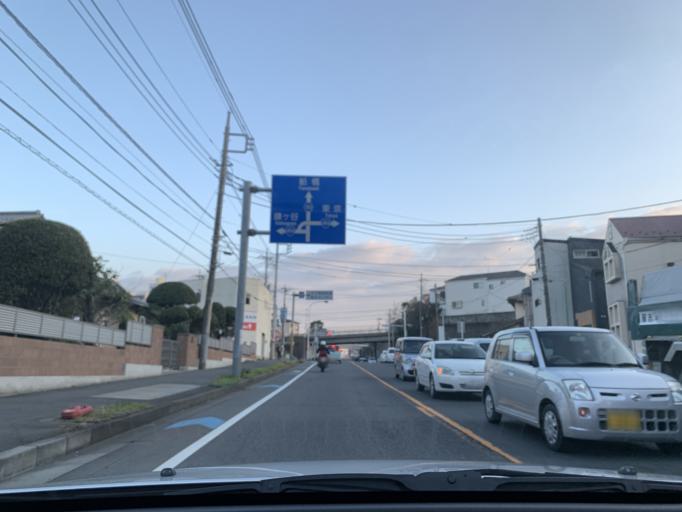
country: JP
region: Chiba
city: Matsudo
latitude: 35.7753
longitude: 139.9050
